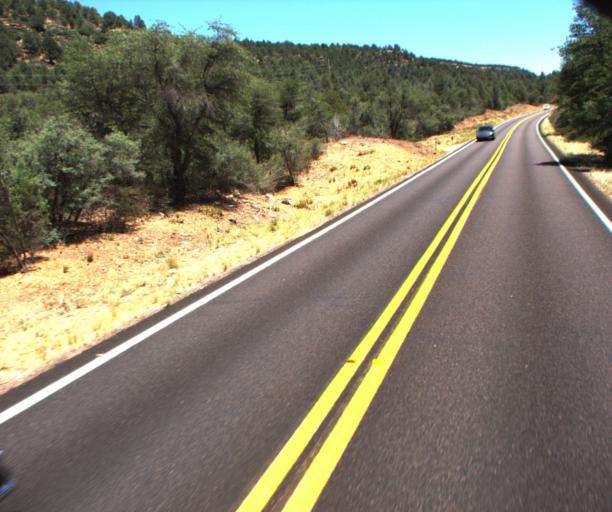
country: US
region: Arizona
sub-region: Gila County
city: Payson
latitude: 34.2855
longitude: -111.3369
